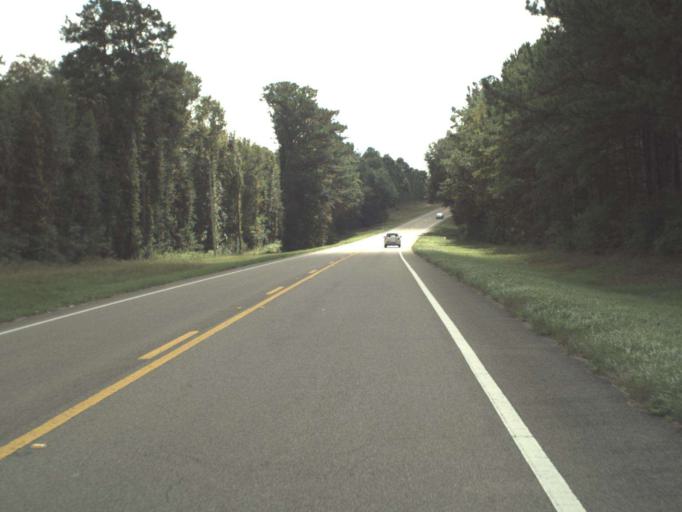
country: US
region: Florida
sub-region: Walton County
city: Freeport
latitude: 30.5551
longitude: -85.9167
